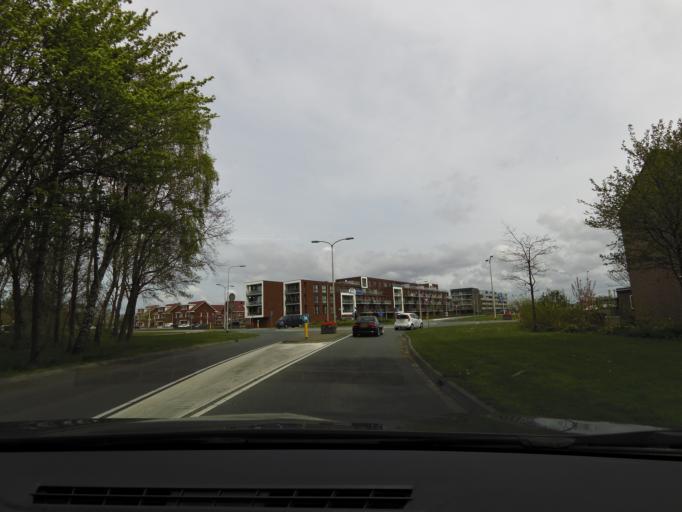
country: NL
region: South Holland
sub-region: Gemeente Katwijk
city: Katwijk aan den Rijn
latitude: 52.2107
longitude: 4.4251
